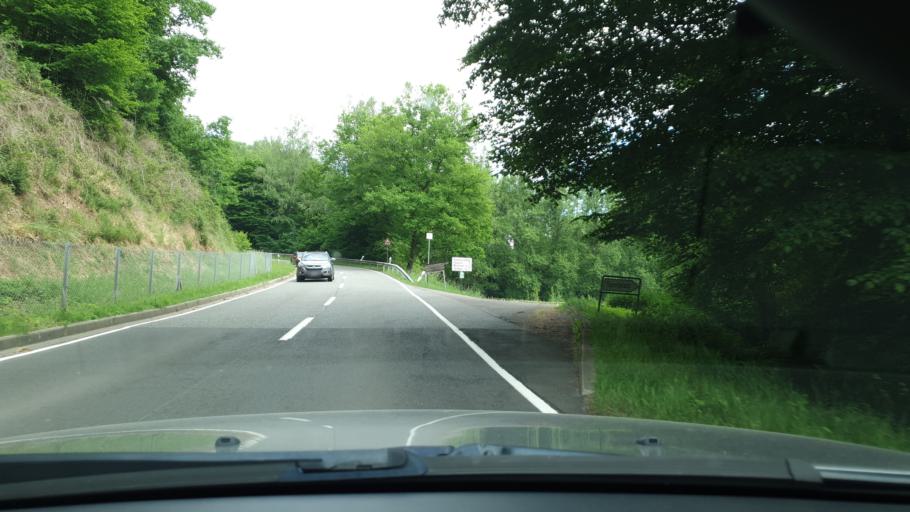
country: DE
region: Rheinland-Pfalz
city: Battweiler
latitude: 49.2779
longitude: 7.4513
